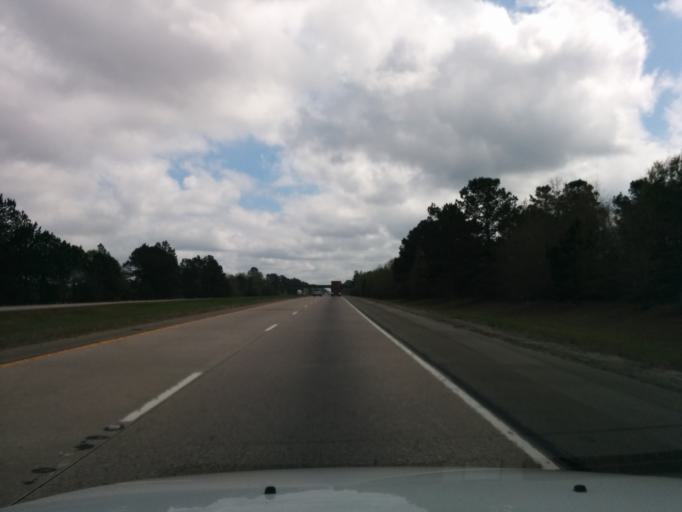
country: US
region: Georgia
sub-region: Bryan County
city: Pembroke
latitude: 32.2054
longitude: -81.4922
